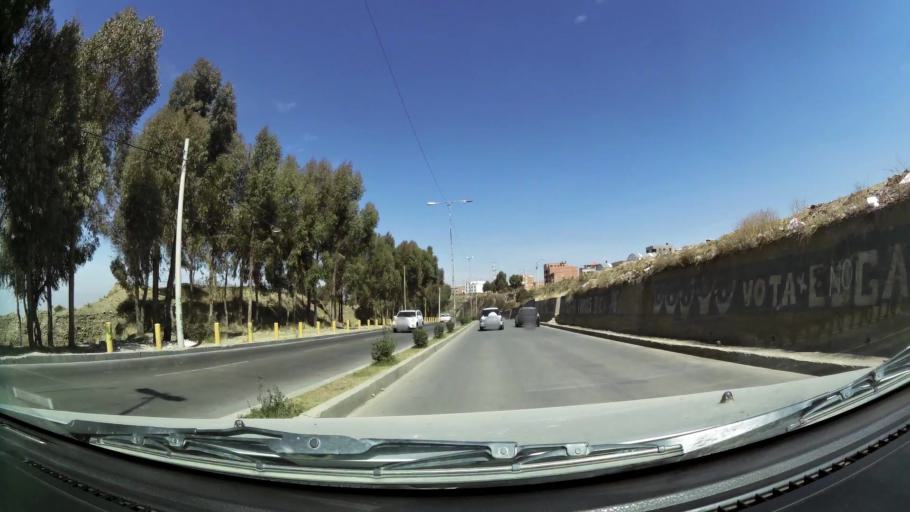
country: BO
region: La Paz
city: La Paz
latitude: -16.5314
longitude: -68.1478
